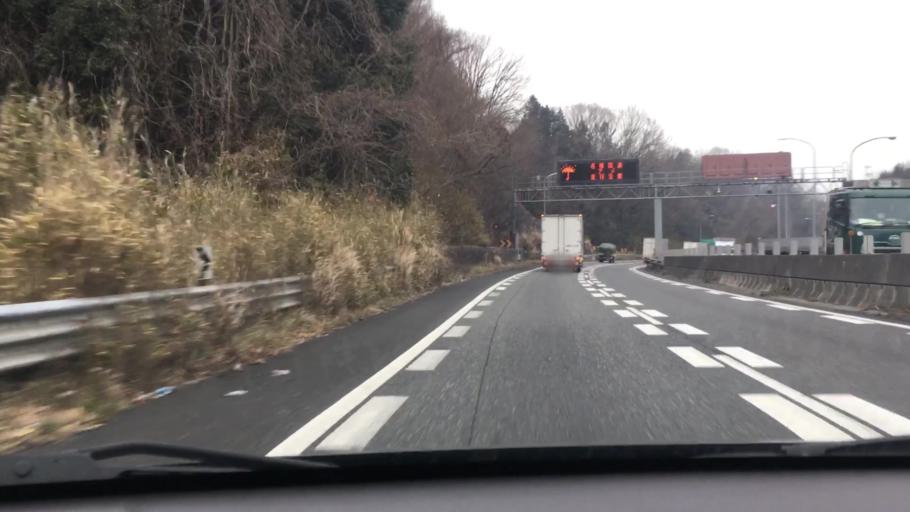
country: JP
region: Mie
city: Nabari
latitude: 34.6882
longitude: 136.0477
